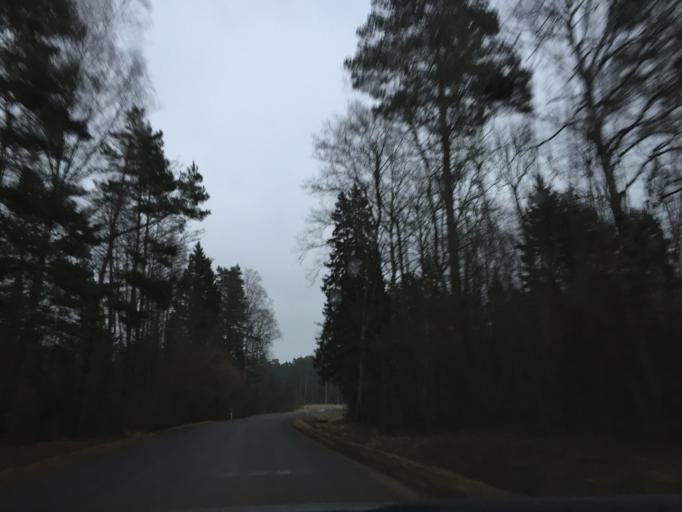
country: EE
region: Saare
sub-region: Kuressaare linn
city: Kuressaare
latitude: 58.6163
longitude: 22.5479
